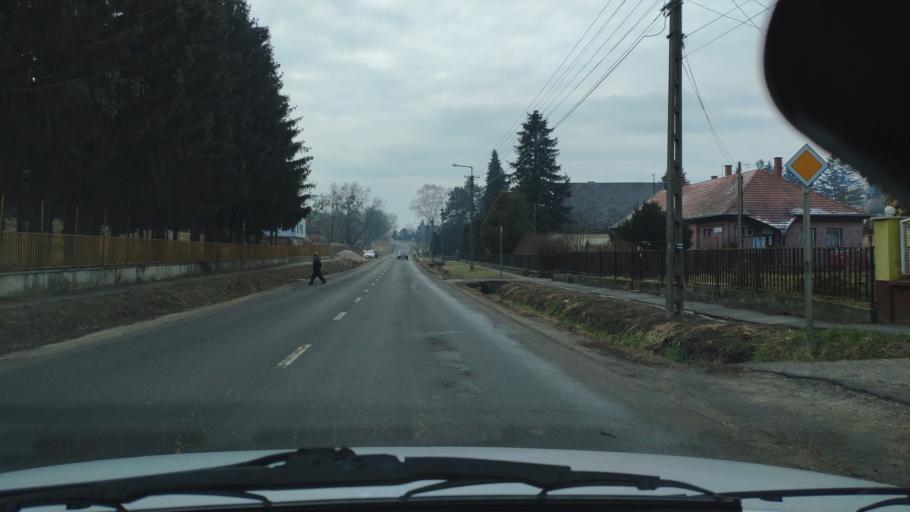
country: HU
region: Zala
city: Nagykanizsa
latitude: 46.4985
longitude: 16.9852
